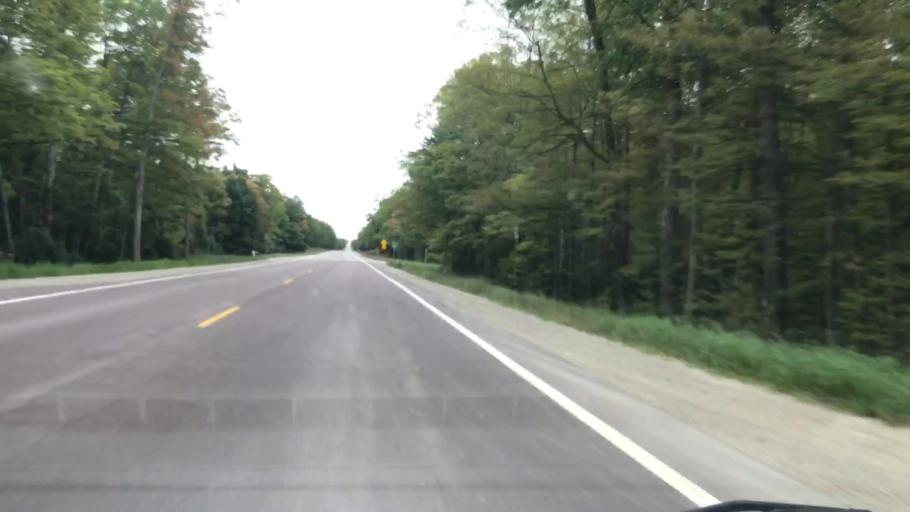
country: US
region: Michigan
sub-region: Luce County
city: Newberry
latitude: 46.2465
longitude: -85.5724
